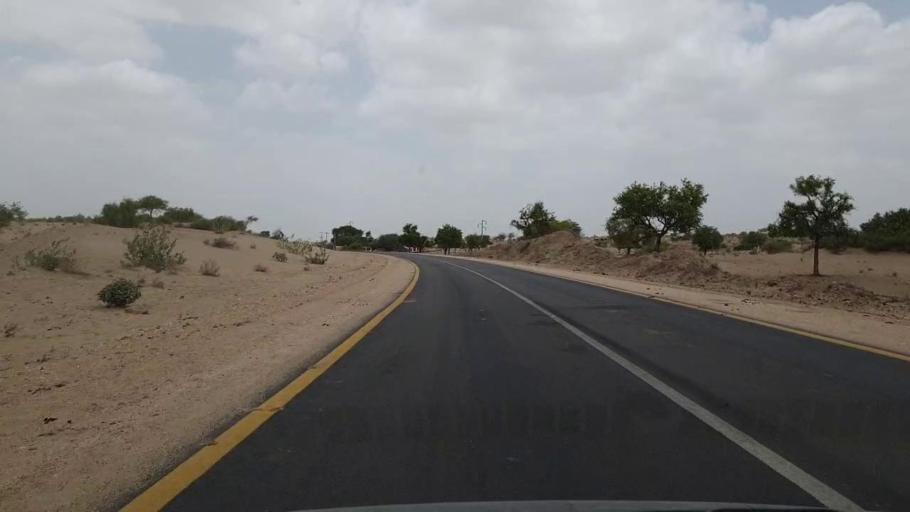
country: PK
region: Sindh
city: Naukot
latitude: 24.8436
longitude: 69.5498
